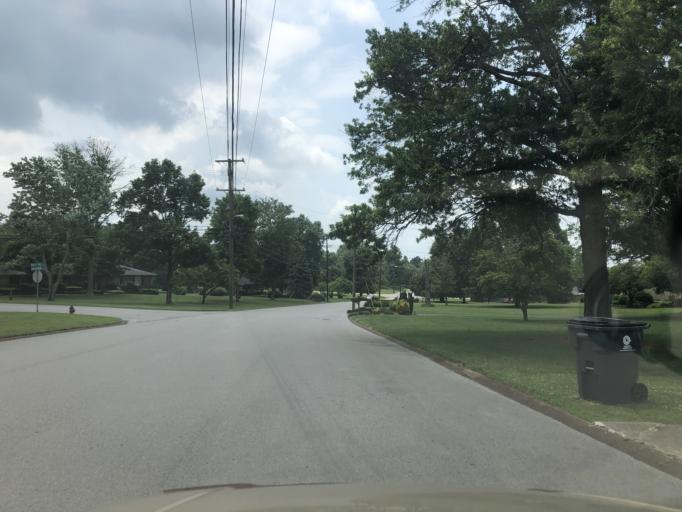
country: US
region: Tennessee
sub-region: Davidson County
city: Lakewood
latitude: 36.2364
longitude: -86.6219
